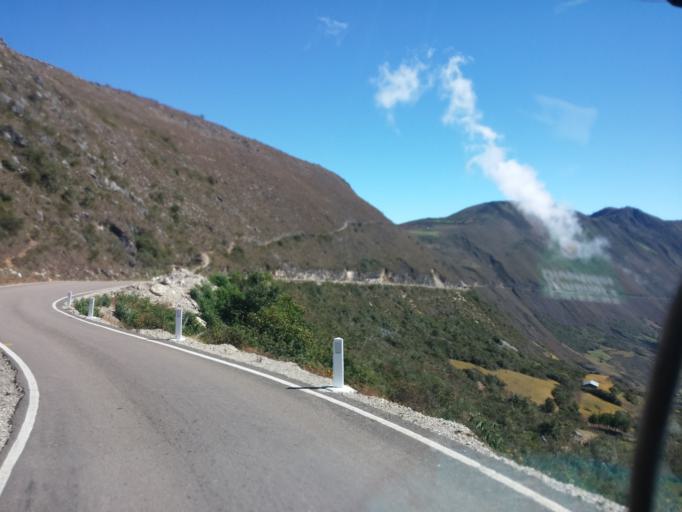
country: PE
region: Cajamarca
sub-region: Provincia de Celendin
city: Celendin
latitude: -6.8699
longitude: -78.1120
